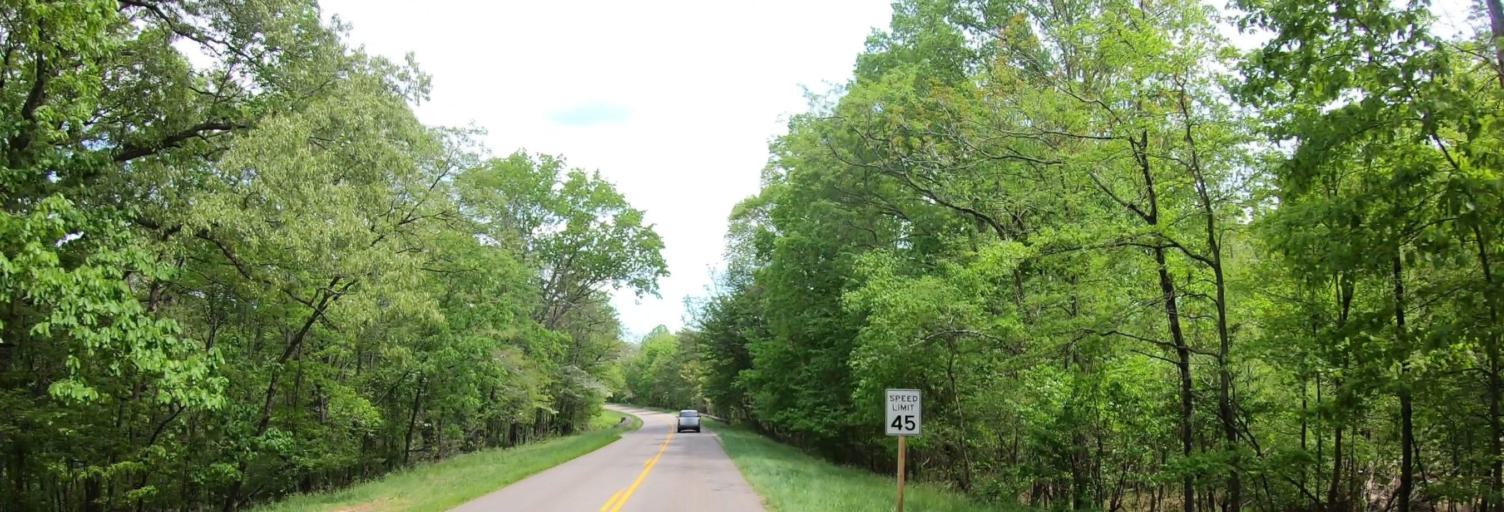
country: US
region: Virginia
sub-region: Roanoke County
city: Narrows
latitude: 37.2233
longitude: -79.9305
